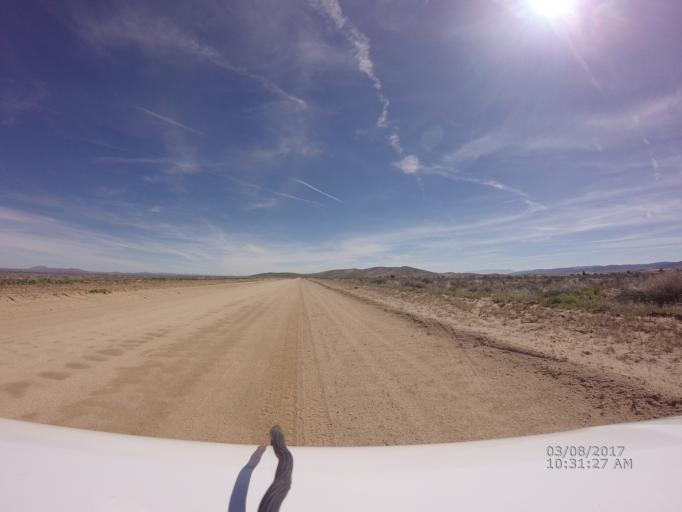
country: US
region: California
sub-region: Los Angeles County
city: Green Valley
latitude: 34.7604
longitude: -118.4441
